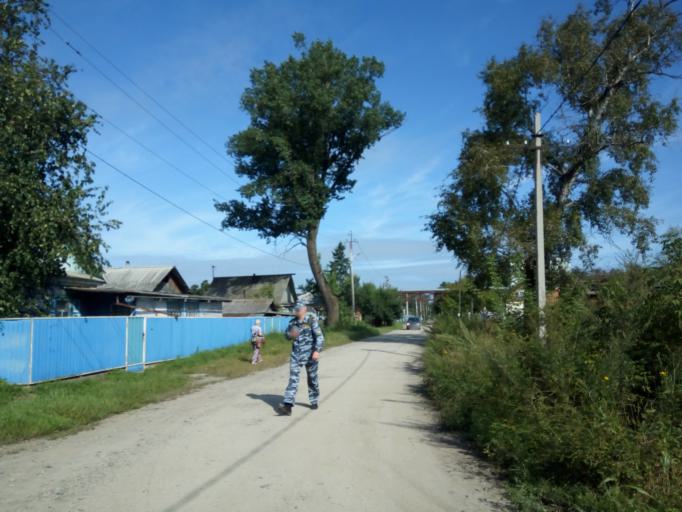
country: RU
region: Primorskiy
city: Dal'nerechensk
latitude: 45.9333
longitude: 133.7417
